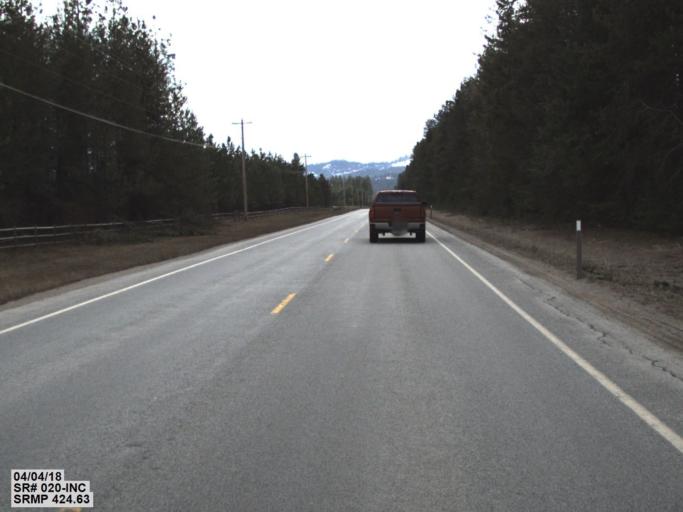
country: US
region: Washington
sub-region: Pend Oreille County
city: Newport
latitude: 48.2638
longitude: -117.2554
